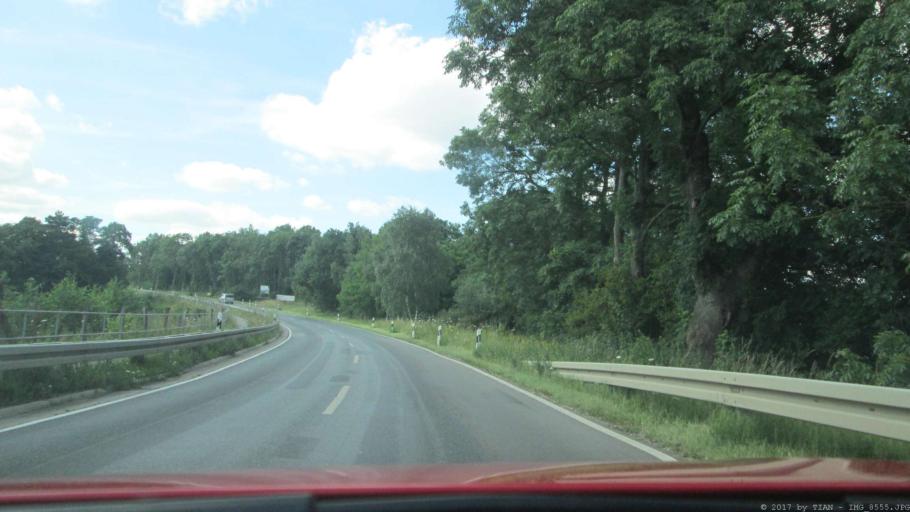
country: DE
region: Lower Saxony
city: Wolfsburg
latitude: 52.3567
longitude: 10.7641
